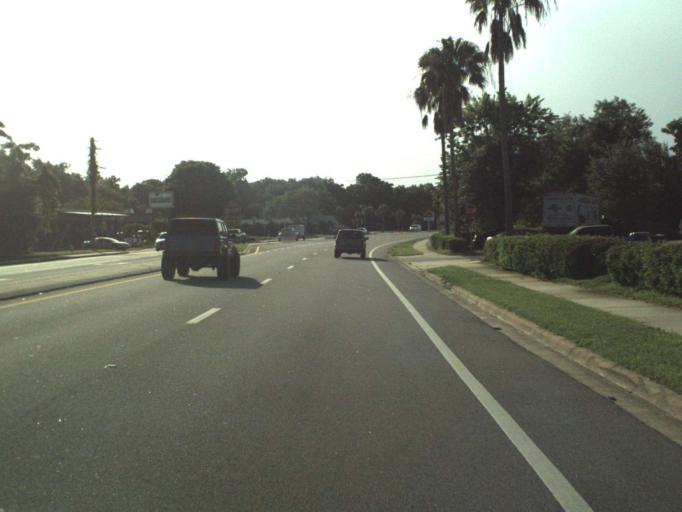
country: US
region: Florida
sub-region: Volusia County
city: Edgewater
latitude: 29.0060
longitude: -80.9166
